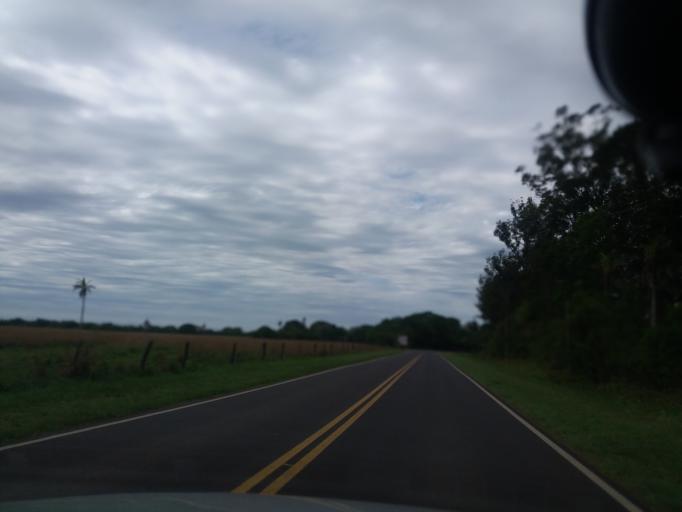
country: AR
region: Corrientes
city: Riachuelo
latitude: -27.4572
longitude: -58.7028
